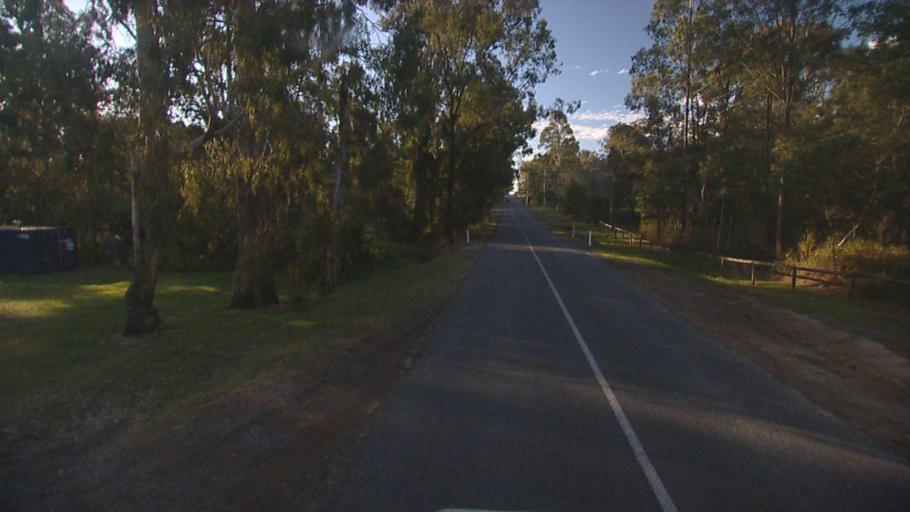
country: AU
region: Queensland
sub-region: Logan
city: Waterford West
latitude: -27.7290
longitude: 153.1466
